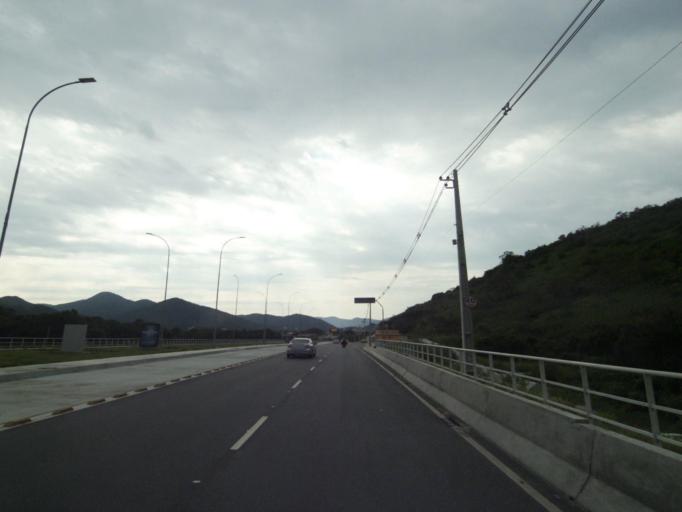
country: BR
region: Rio de Janeiro
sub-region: Niteroi
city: Niteroi
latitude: -22.9366
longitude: -43.0831
